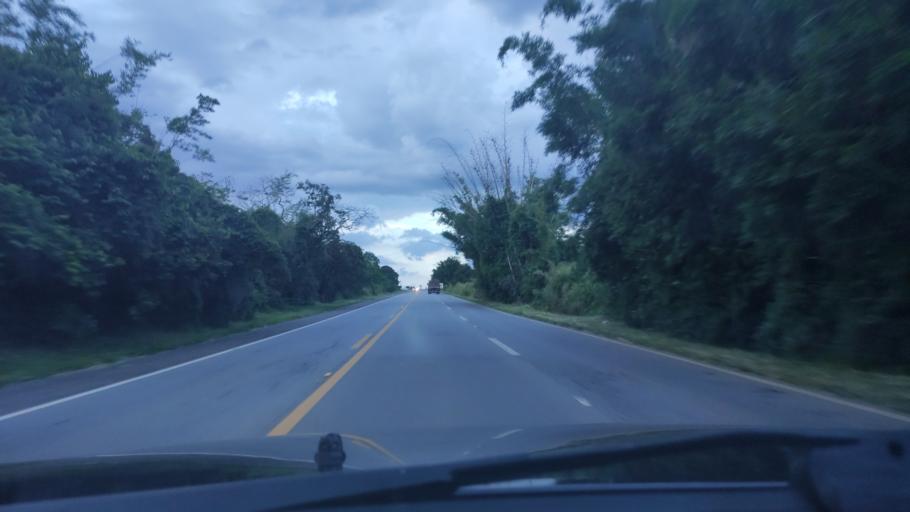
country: BR
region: Sao Paulo
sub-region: Braganca Paulista
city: Braganca Paulista
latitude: -22.8898
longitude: -46.5408
